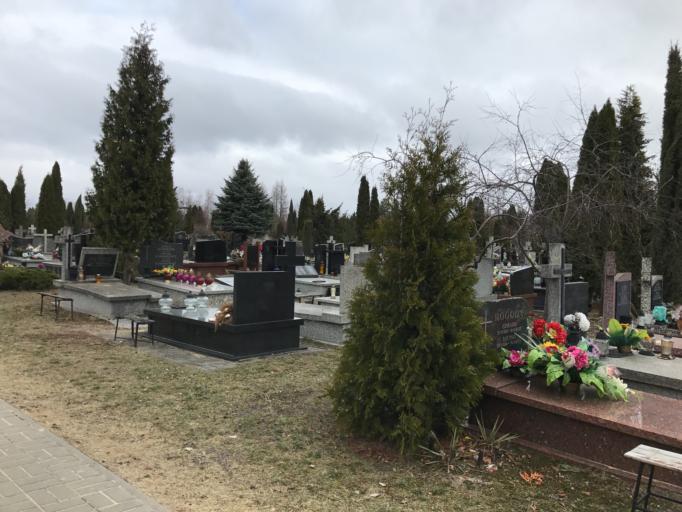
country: PL
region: Masovian Voivodeship
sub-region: Powiat warszawski zachodni
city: Lomianki
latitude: 52.3013
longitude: 20.8896
